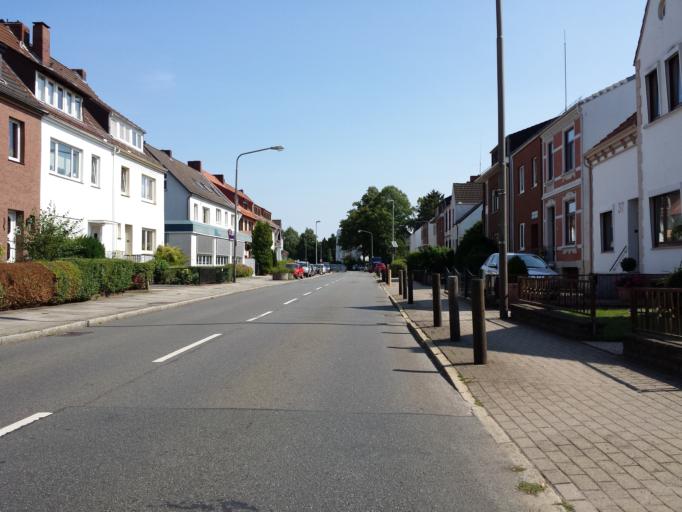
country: DE
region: Bremen
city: Bremen
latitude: 53.0509
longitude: 8.8246
